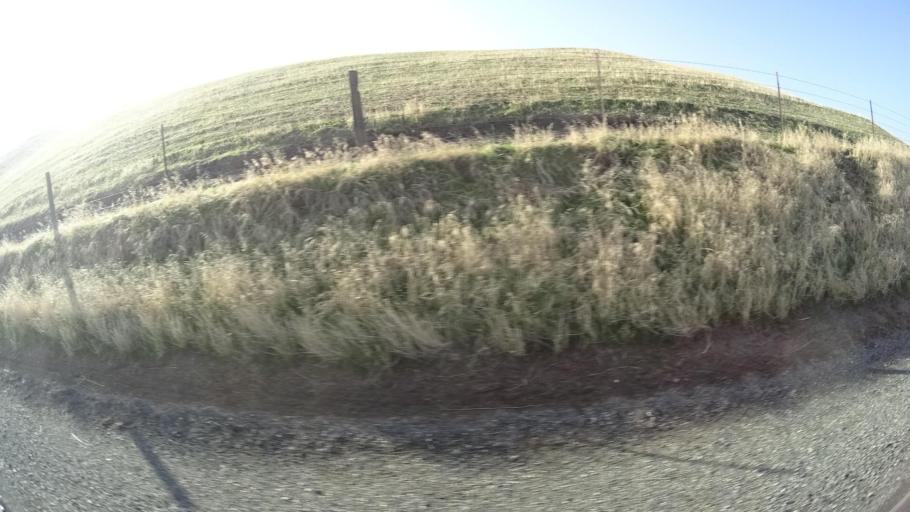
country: US
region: California
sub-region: Tulare County
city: Richgrove
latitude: 35.7489
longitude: -118.9882
